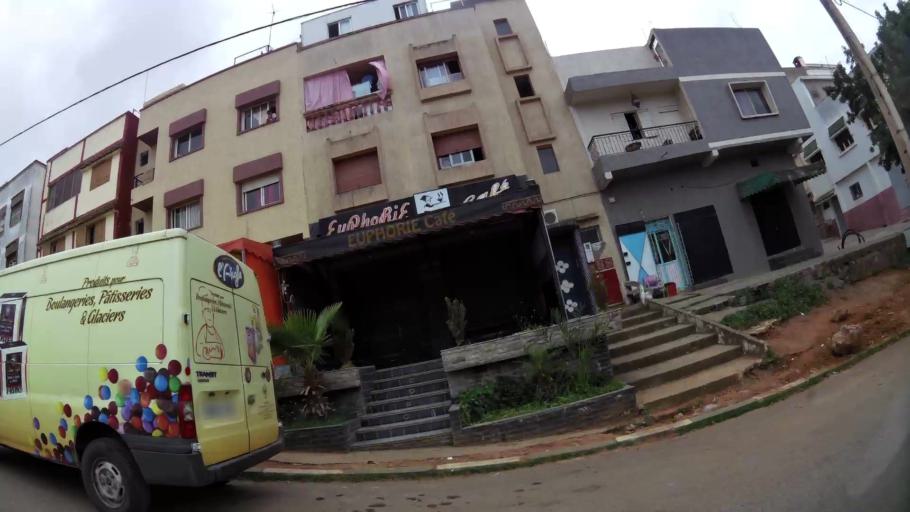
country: MA
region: Rabat-Sale-Zemmour-Zaer
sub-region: Rabat
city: Rabat
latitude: 33.9818
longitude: -6.8146
